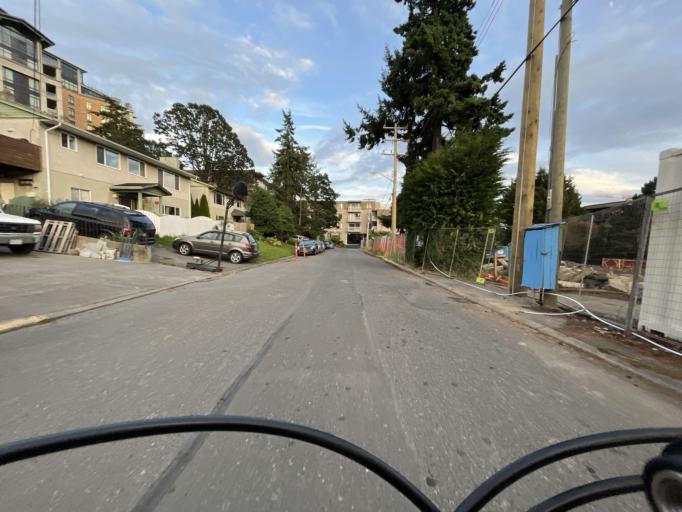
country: CA
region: British Columbia
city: Victoria
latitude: 48.4294
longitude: -123.3979
